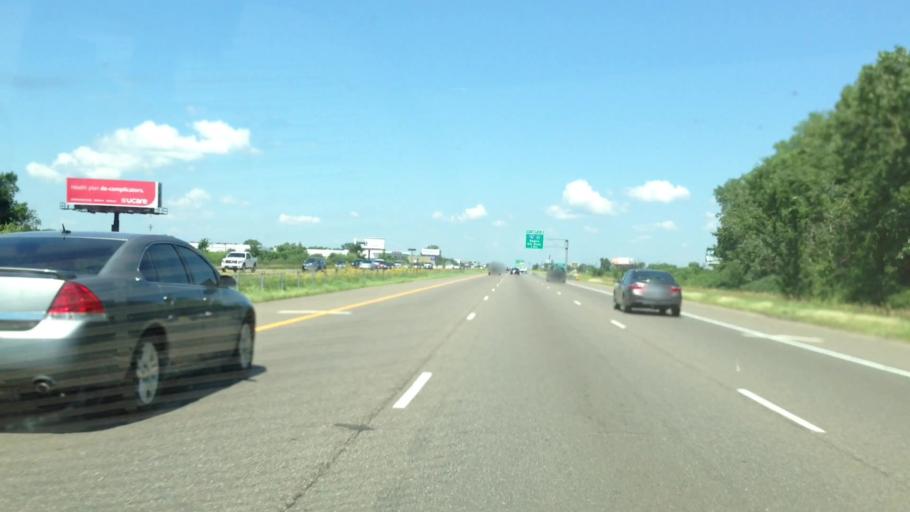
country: US
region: Minnesota
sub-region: Hennepin County
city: Rogers
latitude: 45.1789
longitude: -93.5310
